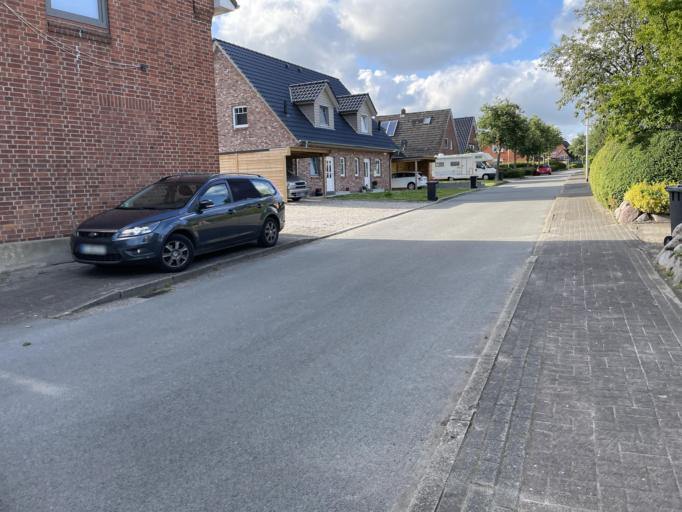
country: DE
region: Schleswig-Holstein
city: Mildstedt
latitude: 54.4572
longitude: 9.0966
